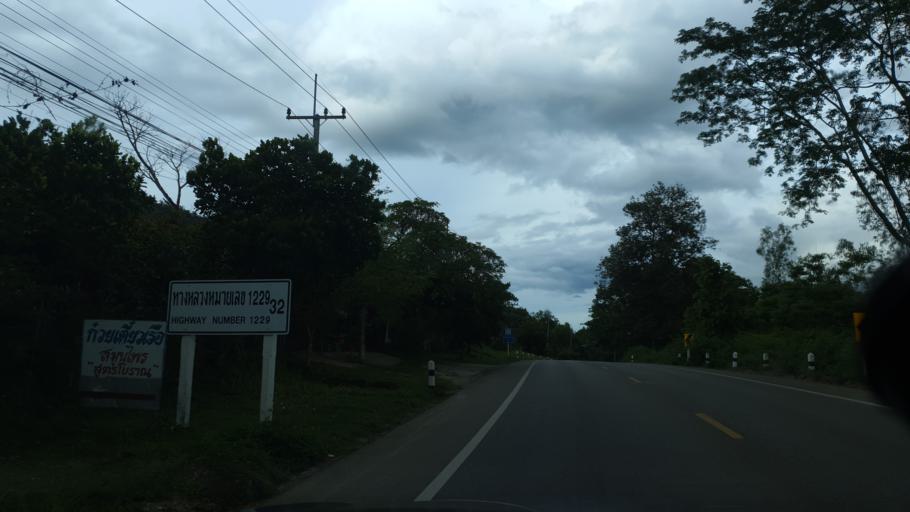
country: TH
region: Lamphun
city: Mae Tha
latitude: 18.4905
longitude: 99.1854
